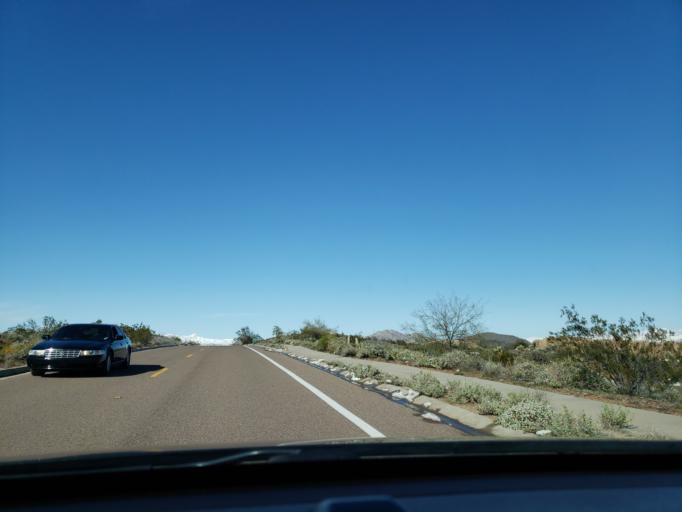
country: US
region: Arizona
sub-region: Maricopa County
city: Carefree
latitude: 33.7241
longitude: -111.8264
